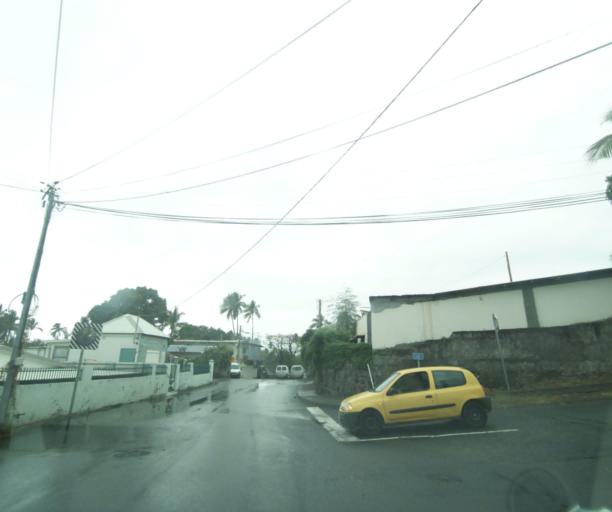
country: RE
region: Reunion
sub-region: Reunion
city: Saint-Paul
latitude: -21.0124
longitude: 55.2760
